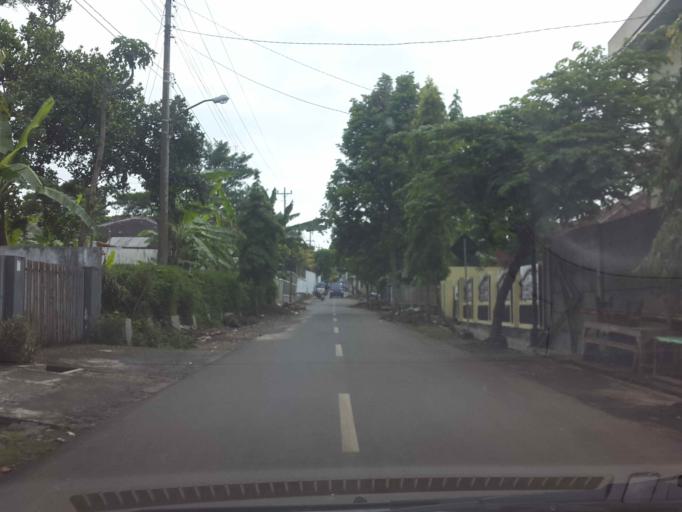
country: ID
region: Central Java
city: Salatiga
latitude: -7.3318
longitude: 110.4993
